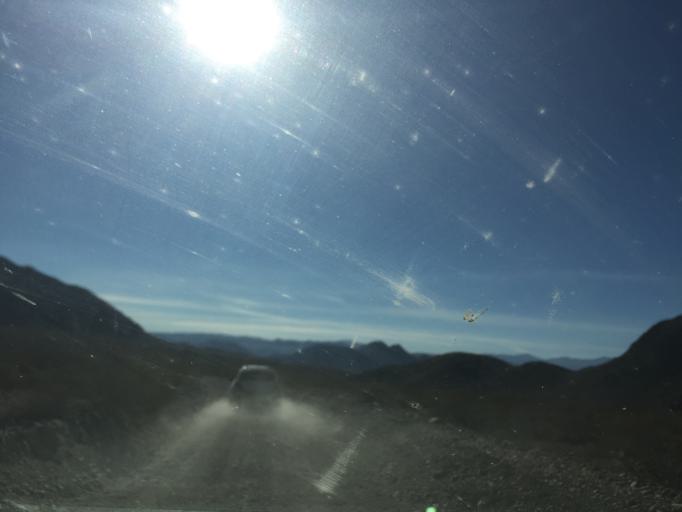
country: US
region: California
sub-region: Inyo County
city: Lone Pine
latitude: 36.7720
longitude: -117.5330
